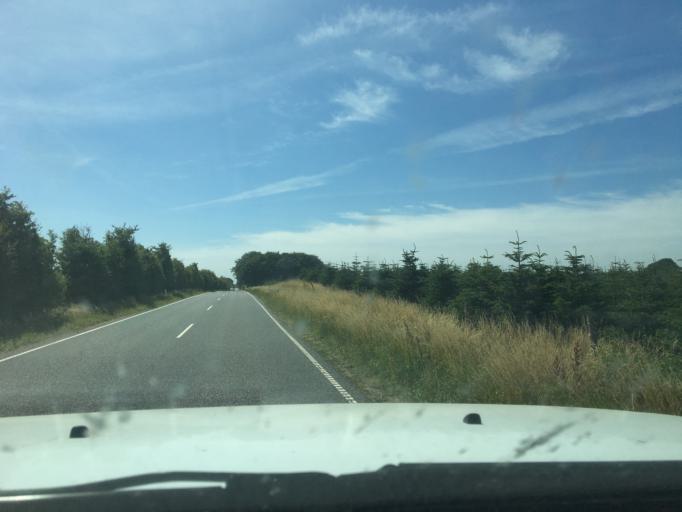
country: DK
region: Central Jutland
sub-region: Viborg Kommune
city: Bjerringbro
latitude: 56.5250
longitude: 9.6474
